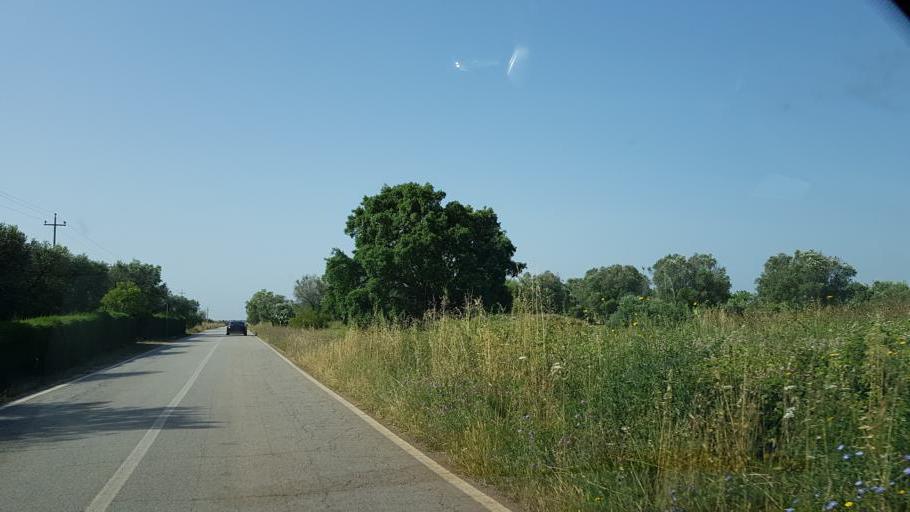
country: IT
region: Apulia
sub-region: Provincia di Brindisi
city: San Pancrazio Salentino
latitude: 40.4516
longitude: 17.8407
